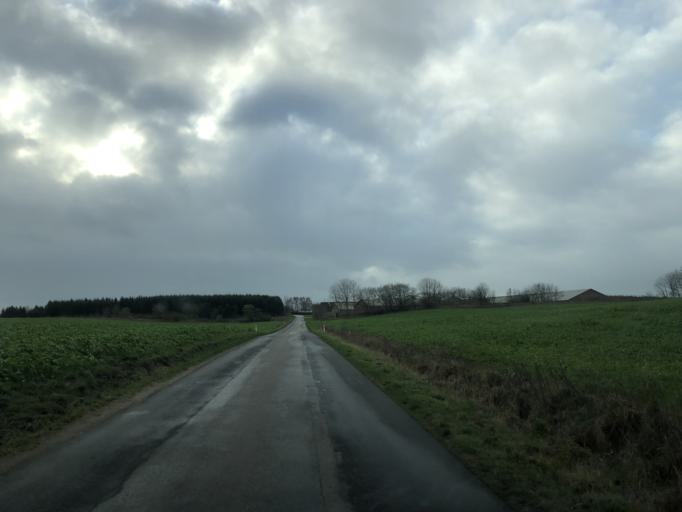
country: DK
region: North Denmark
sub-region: Rebild Kommune
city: Stovring
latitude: 56.9232
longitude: 9.8047
